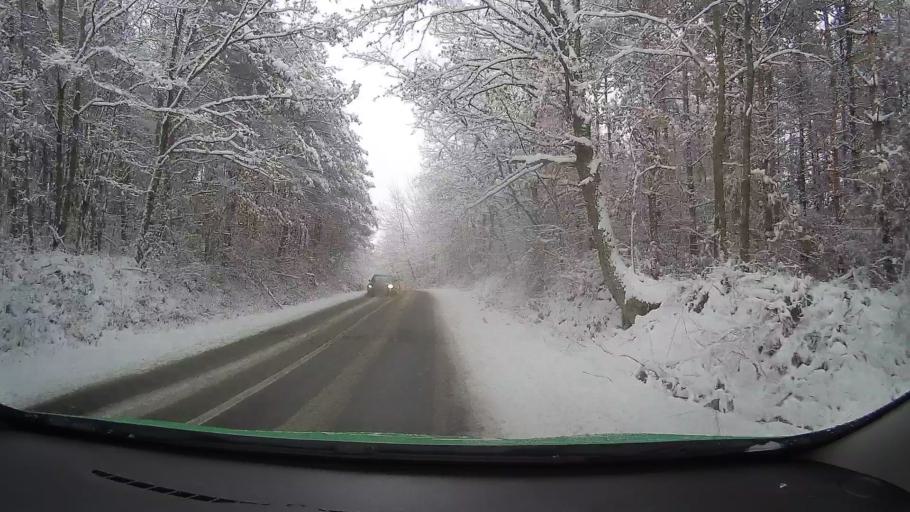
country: RO
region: Hunedoara
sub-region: Comuna Teliucu Inferior
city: Teliucu Inferior
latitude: 45.6773
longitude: 22.9131
